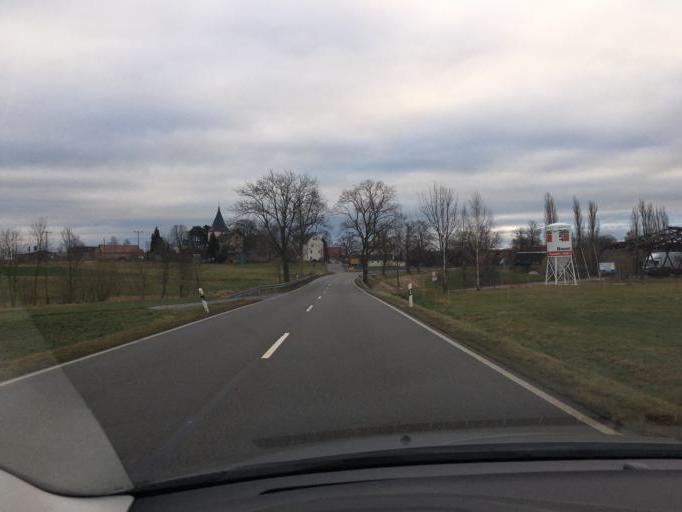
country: DE
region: Thuringia
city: Juckelberg
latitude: 50.9668
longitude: 12.6513
